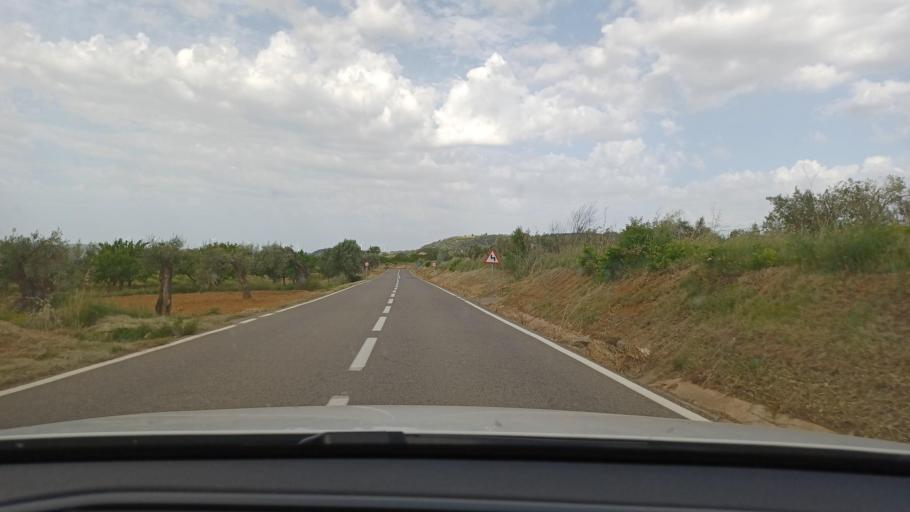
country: ES
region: Catalonia
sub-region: Provincia de Tarragona
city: Gandesa
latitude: 41.0500
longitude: 0.4124
